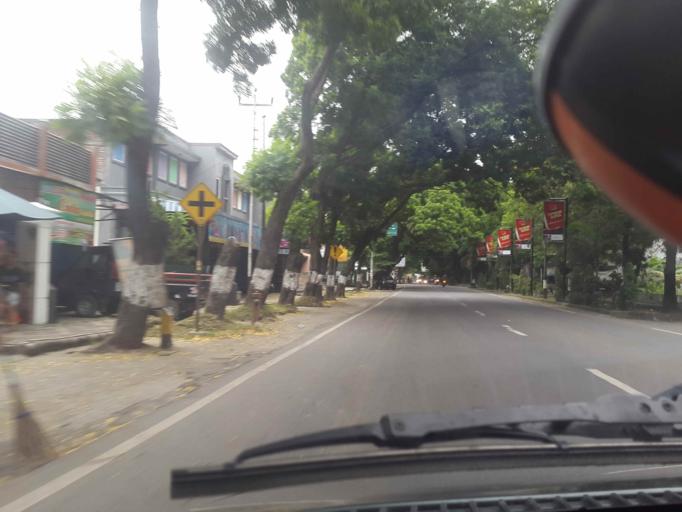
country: ID
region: Central Java
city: Sragen
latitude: -7.4316
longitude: 111.0239
